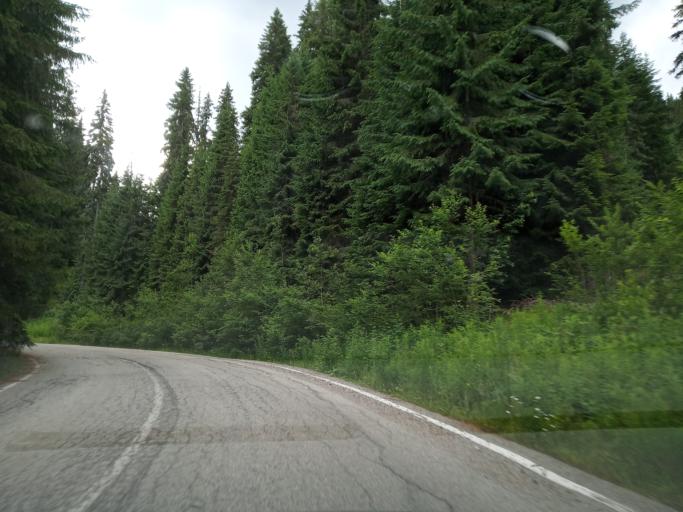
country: RO
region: Valcea
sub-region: Comuna Voineasa
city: Voineasa
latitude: 45.4255
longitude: 23.7464
